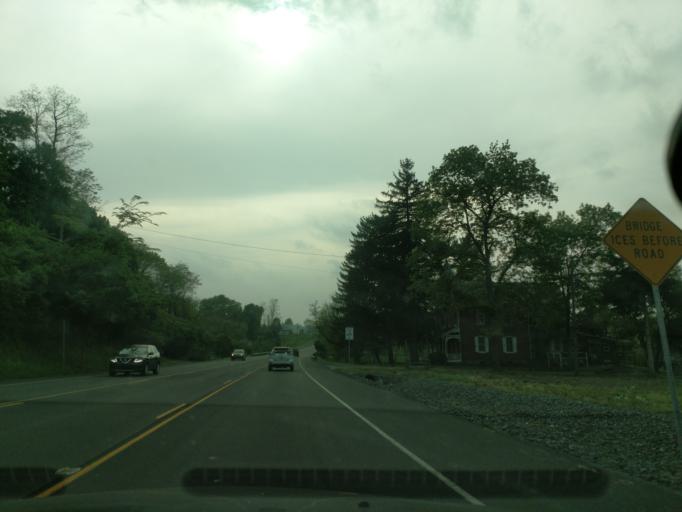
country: US
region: Pennsylvania
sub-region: Berks County
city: Wernersville
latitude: 40.3263
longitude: -76.0586
